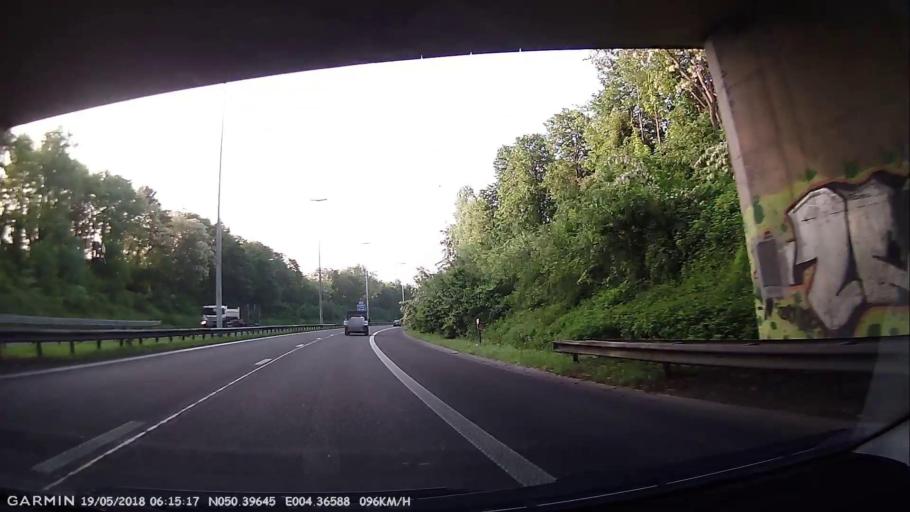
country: BE
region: Wallonia
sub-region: Province du Hainaut
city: Courcelles
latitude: 50.3963
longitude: 4.3661
